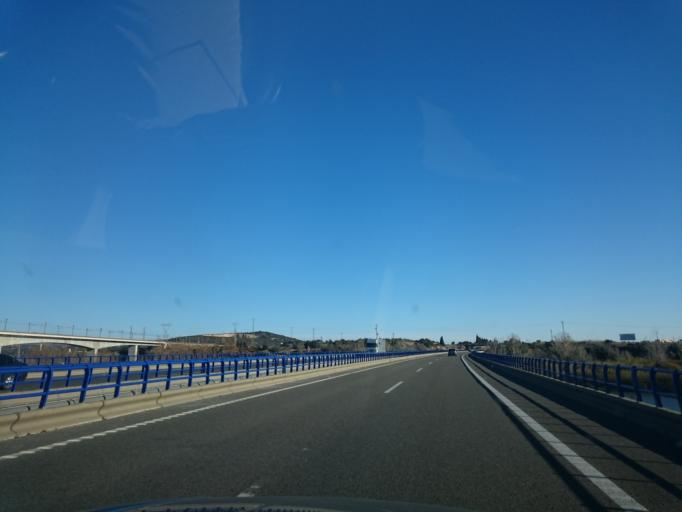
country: ES
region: Catalonia
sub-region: Provincia de Tarragona
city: Amposta
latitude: 40.7274
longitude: 0.5724
